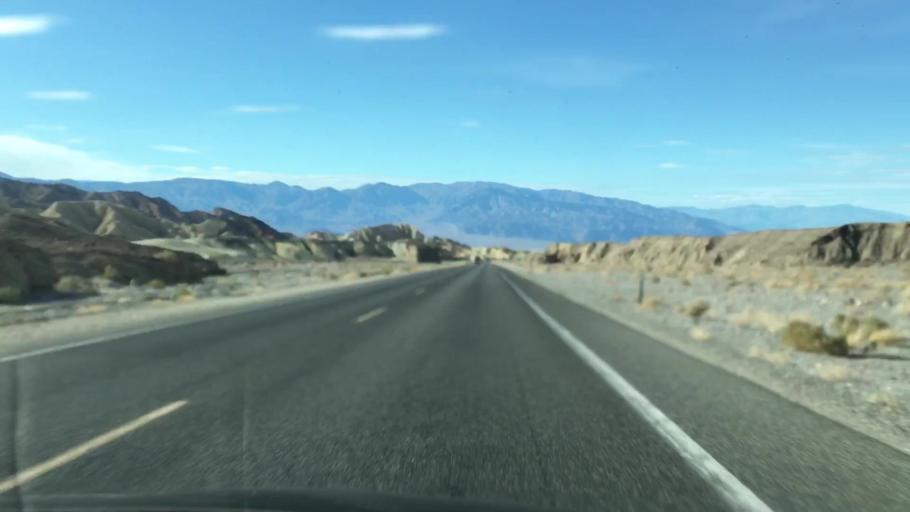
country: US
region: Nevada
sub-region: Nye County
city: Beatty
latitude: 36.4020
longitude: -116.7780
